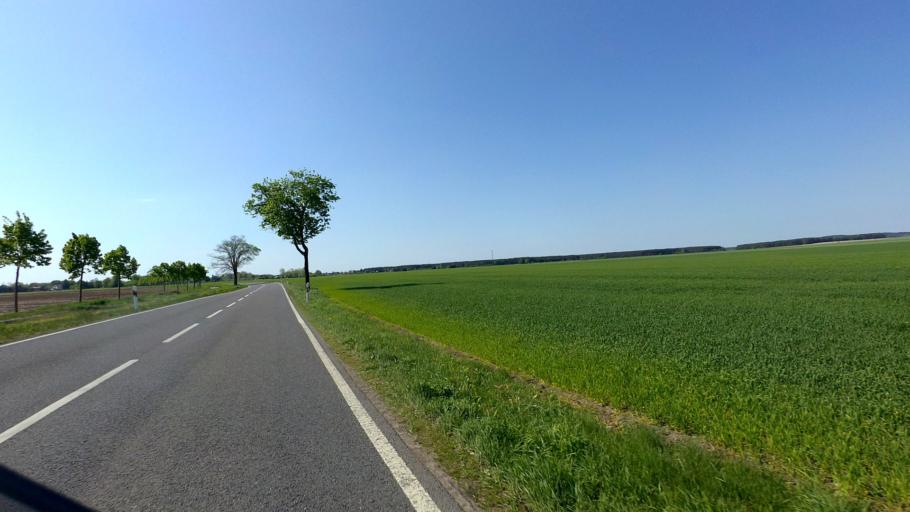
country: DE
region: Brandenburg
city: Schlepzig
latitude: 52.0536
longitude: 13.9800
